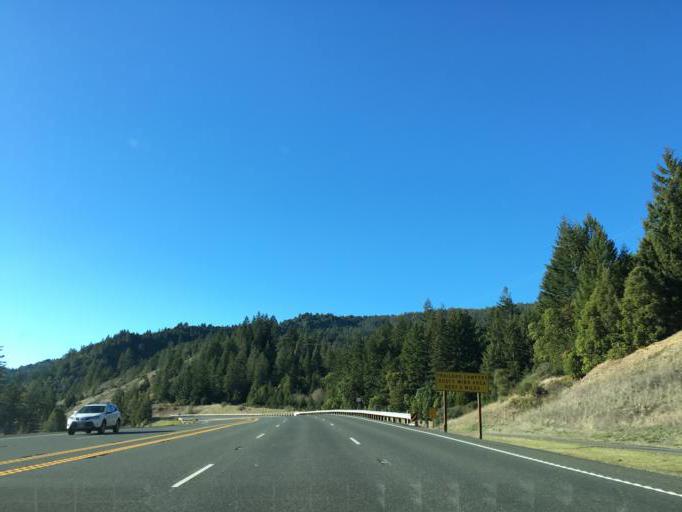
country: US
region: California
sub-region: Mendocino County
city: Laytonville
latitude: 39.8342
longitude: -123.6298
